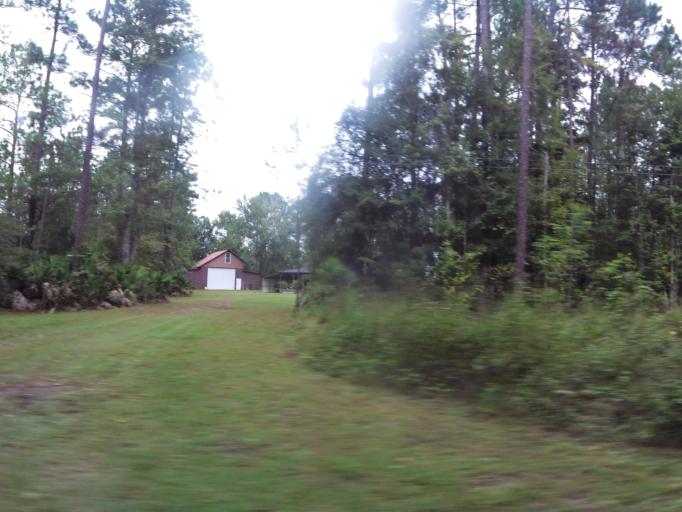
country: US
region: Florida
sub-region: Clay County
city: Bellair-Meadowbrook Terrace
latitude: 30.2032
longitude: -81.8487
